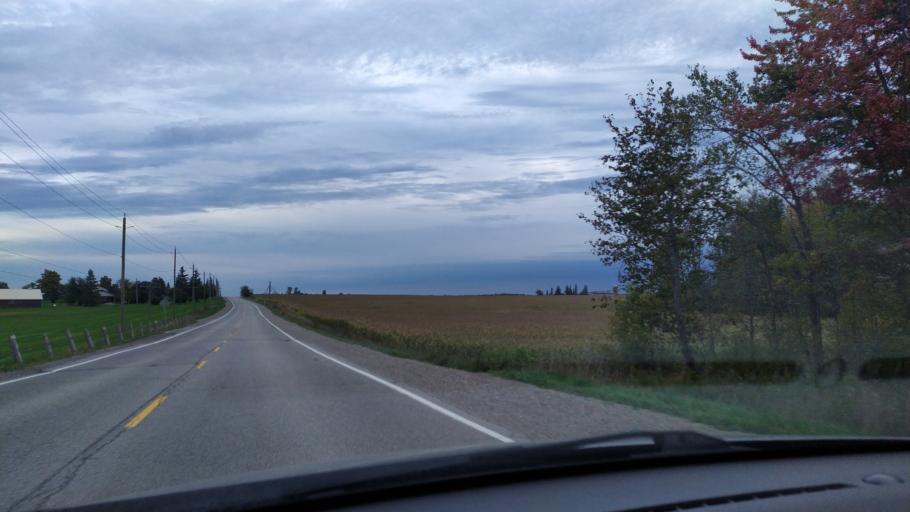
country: CA
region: Ontario
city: Stratford
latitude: 43.5076
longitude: -80.7594
